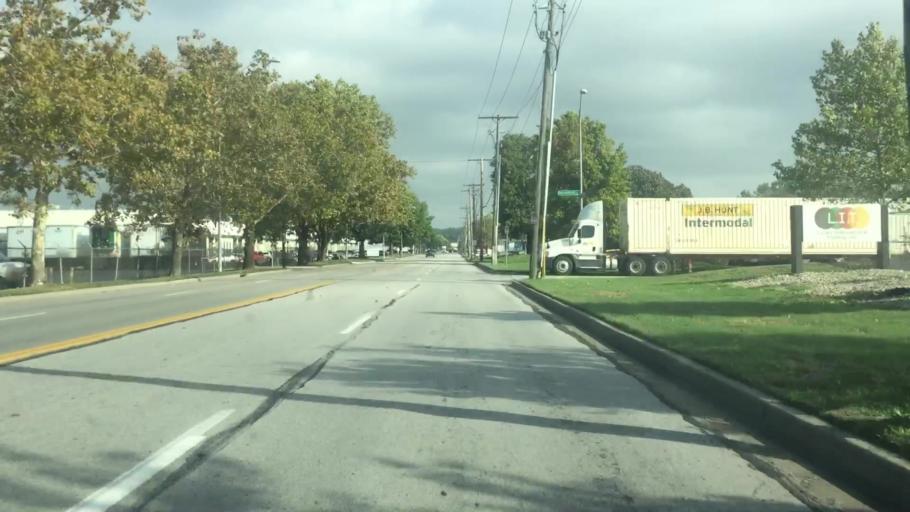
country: US
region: Missouri
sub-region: Clay County
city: North Kansas City
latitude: 39.1329
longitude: -94.5140
